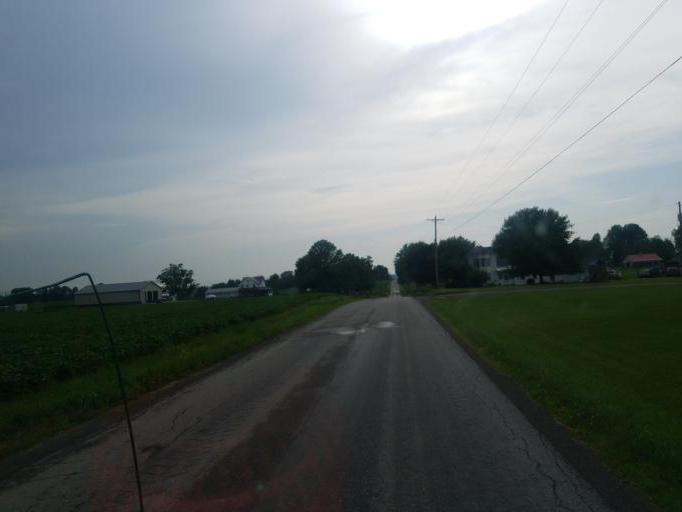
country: US
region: Ohio
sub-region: Wayne County
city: West Salem
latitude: 40.9009
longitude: -82.0952
